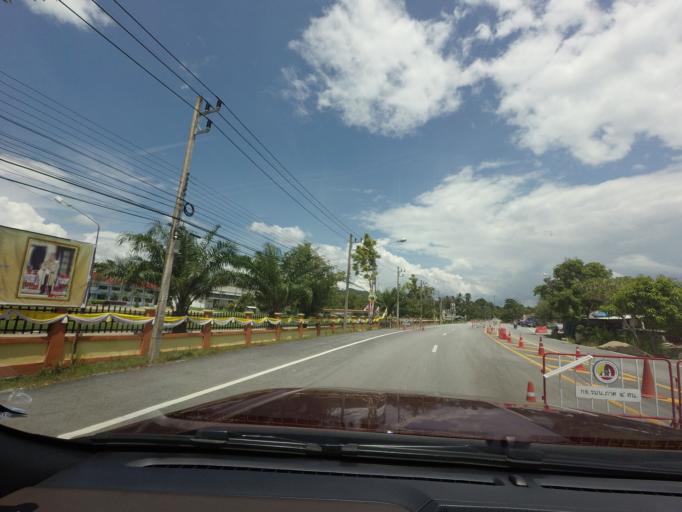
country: TH
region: Narathiwat
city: Chanae
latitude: 6.0981
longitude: 101.6924
